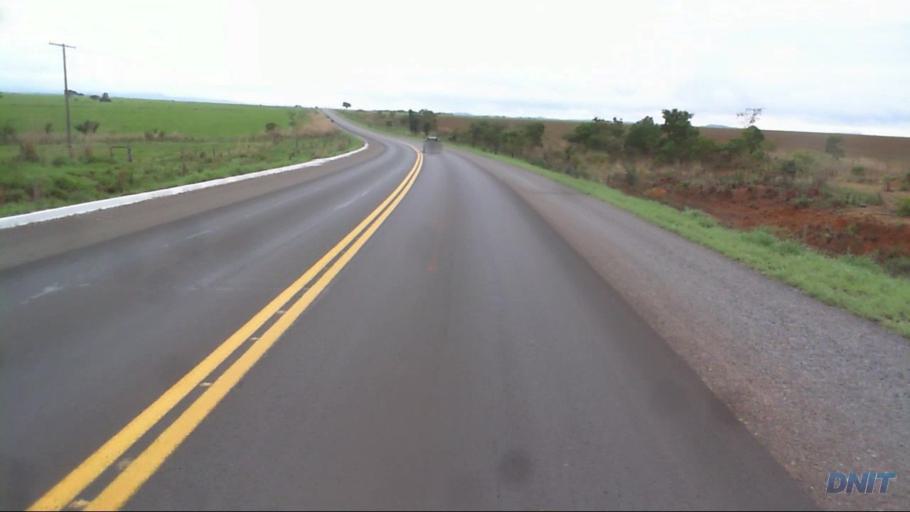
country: BR
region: Goias
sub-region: Padre Bernardo
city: Padre Bernardo
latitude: -15.1749
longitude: -48.3805
